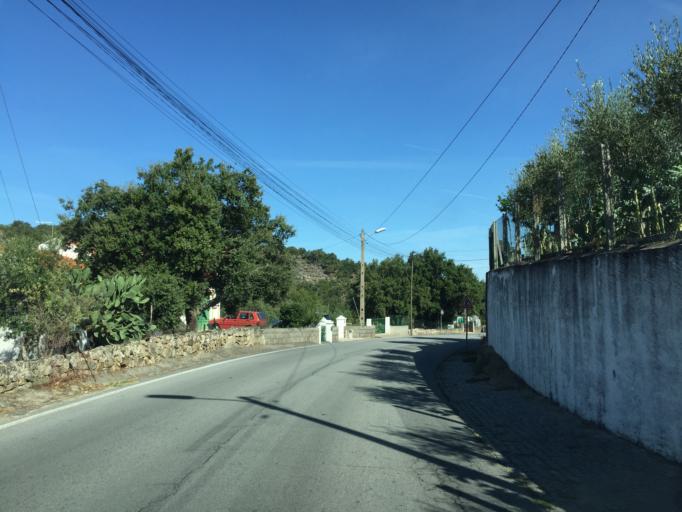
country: PT
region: Portalegre
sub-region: Marvao
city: Marvao
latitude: 39.4146
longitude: -7.3535
